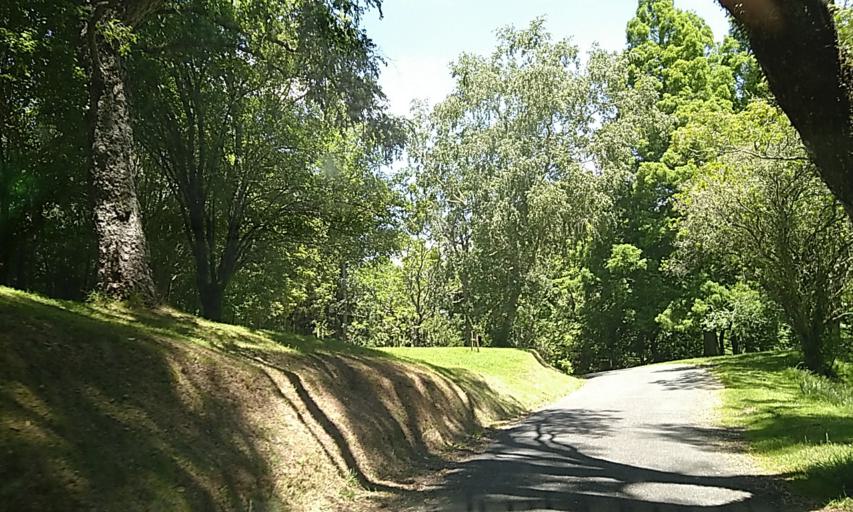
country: NZ
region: Bay of Plenty
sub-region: Tauranga City
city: Tauranga
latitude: -37.8105
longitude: 176.0447
